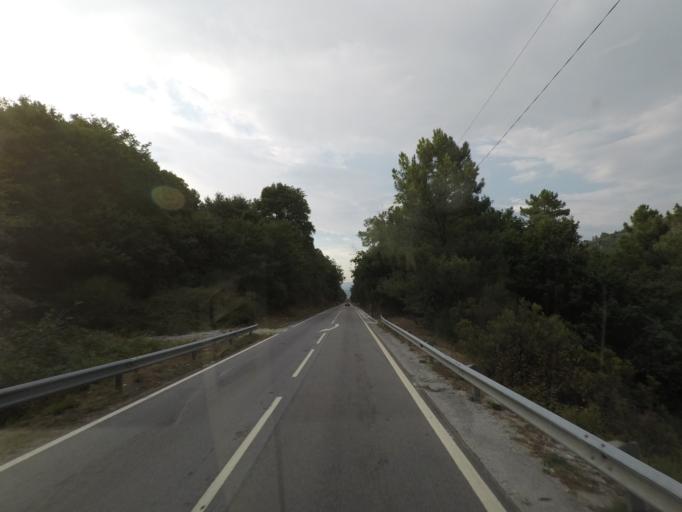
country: PT
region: Porto
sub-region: Baiao
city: Baiao
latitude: 41.2199
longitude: -7.9899
